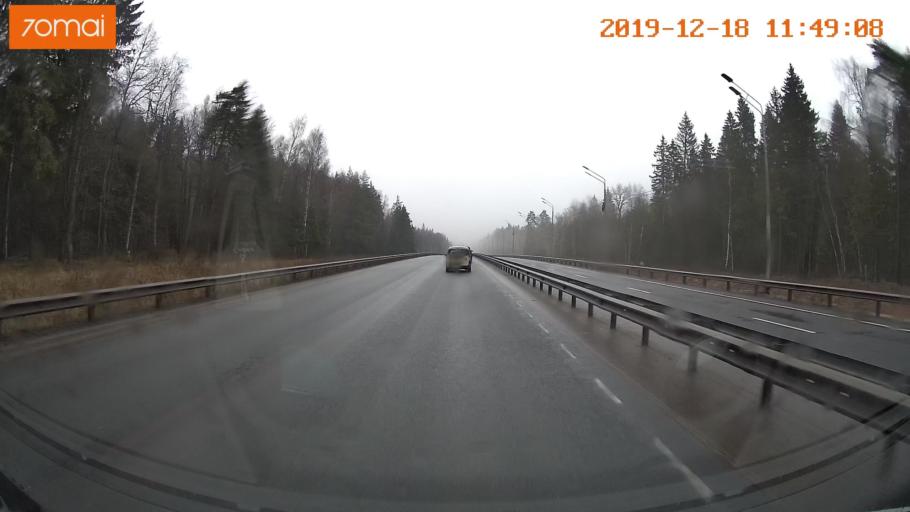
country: RU
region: Moskovskaya
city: Yershovo
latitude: 55.7749
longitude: 36.9093
